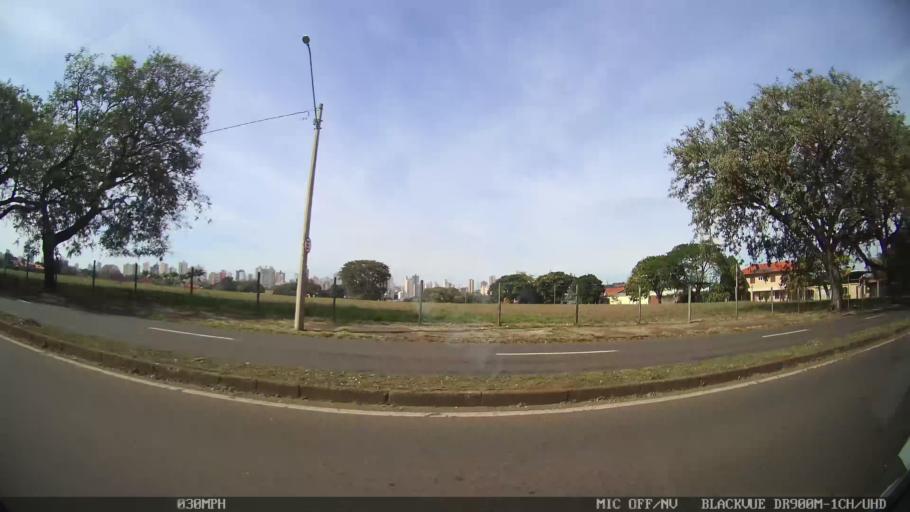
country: BR
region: Sao Paulo
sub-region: Piracicaba
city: Piracicaba
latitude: -22.7205
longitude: -47.6633
